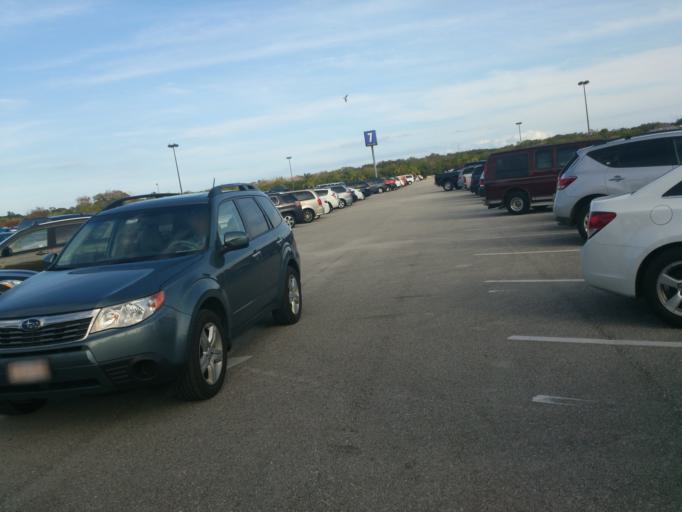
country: US
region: Florida
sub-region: Brevard County
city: Merritt Island
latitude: 28.5192
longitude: -80.6818
